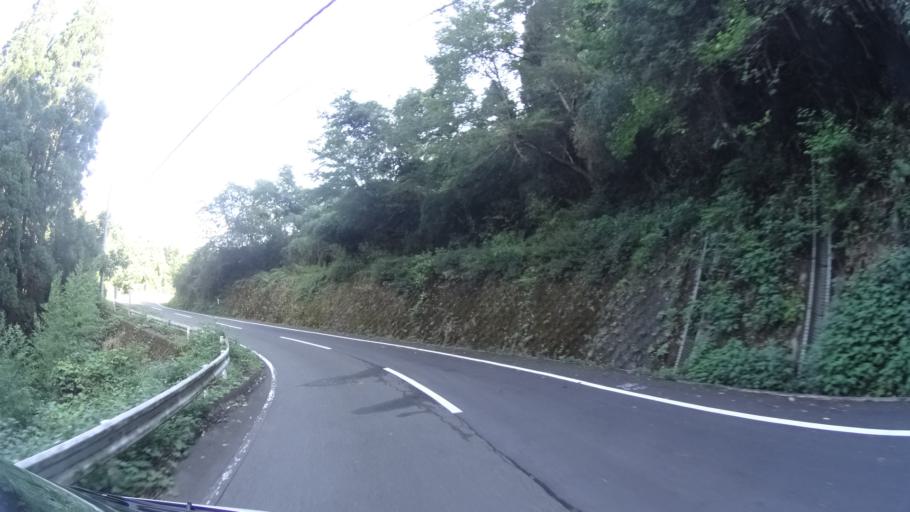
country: JP
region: Kyoto
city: Ayabe
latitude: 35.2800
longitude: 135.3302
